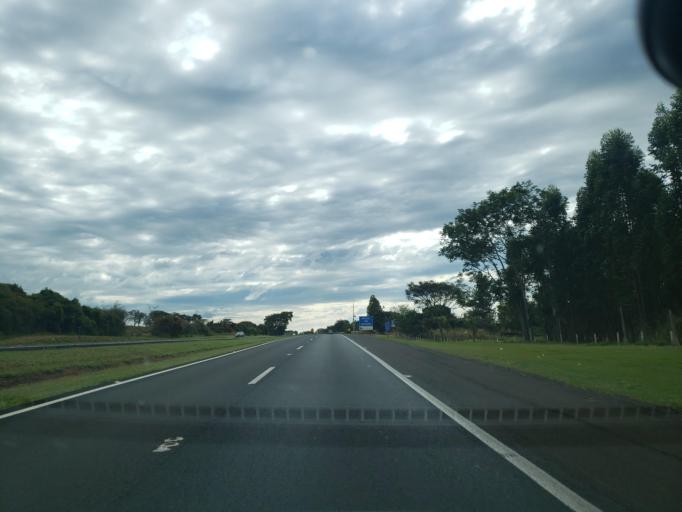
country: BR
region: Sao Paulo
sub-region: Bauru
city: Bauru
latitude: -22.2012
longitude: -49.1859
